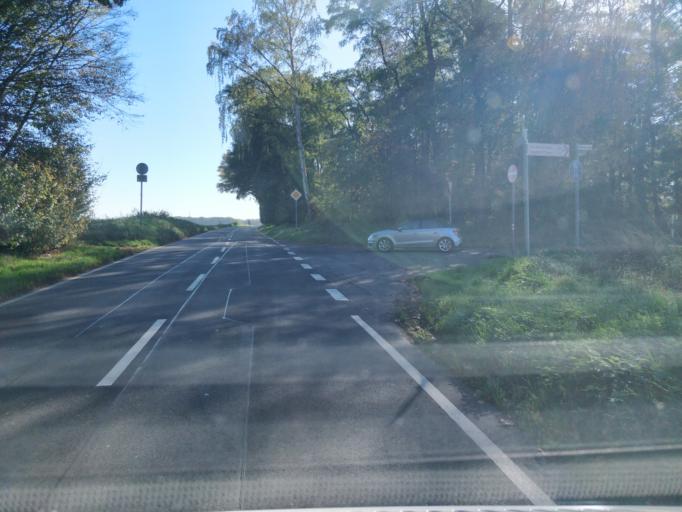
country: DE
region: North Rhine-Westphalia
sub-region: Regierungsbezirk Koln
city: Sinnersdorf
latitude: 51.0417
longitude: 6.8640
